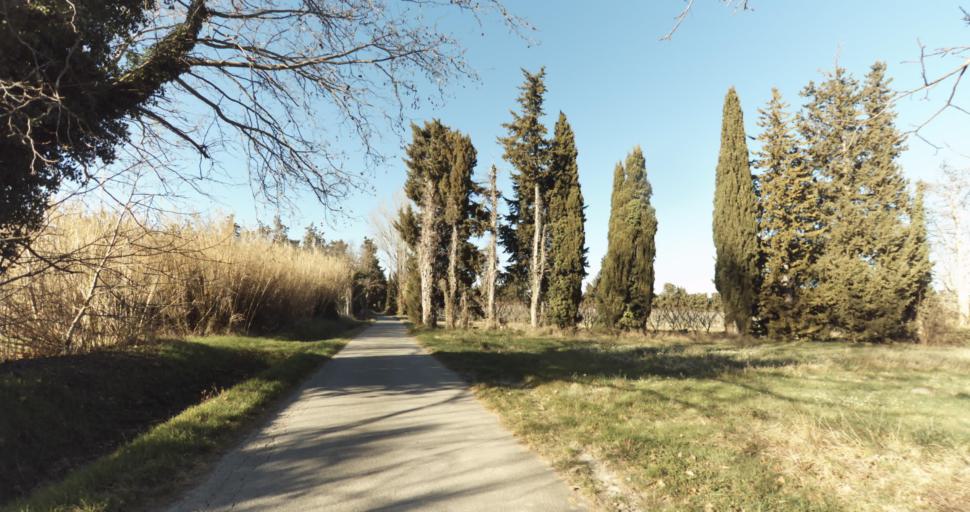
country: FR
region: Provence-Alpes-Cote d'Azur
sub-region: Departement des Bouches-du-Rhone
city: Barbentane
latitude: 43.9180
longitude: 4.7520
